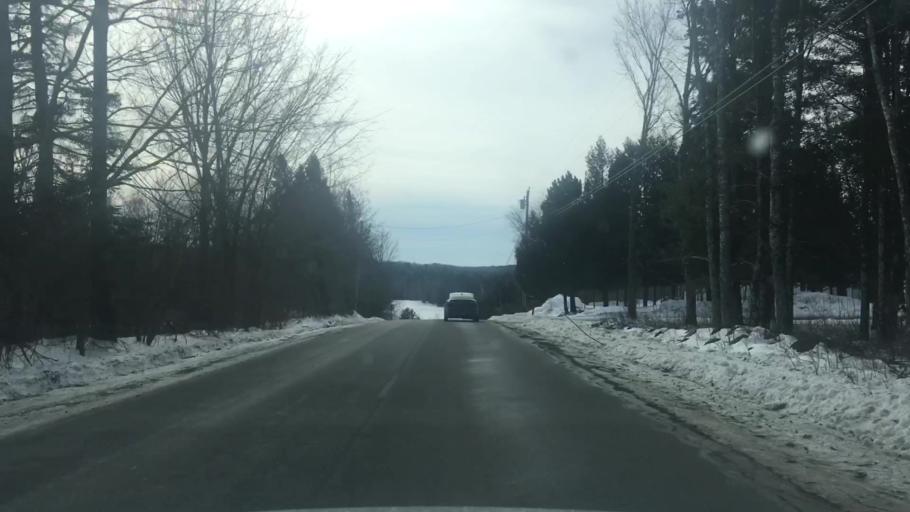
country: US
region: Maine
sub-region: Hancock County
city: Orland
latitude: 44.5985
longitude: -68.7228
